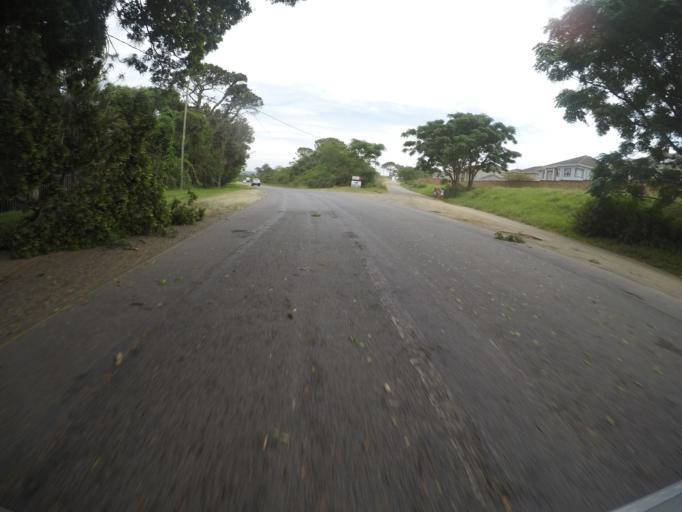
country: ZA
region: Eastern Cape
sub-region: Buffalo City Metropolitan Municipality
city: East London
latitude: -32.9479
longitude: 27.9273
